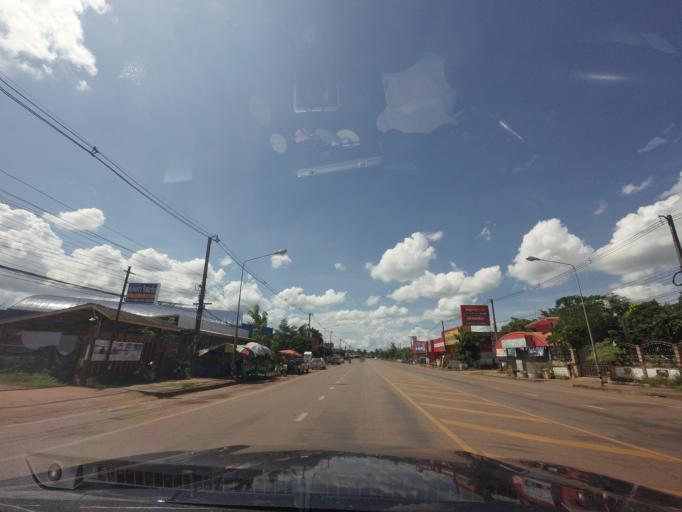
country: TH
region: Changwat Udon Thani
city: Ban Dung
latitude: 17.7034
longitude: 103.2547
